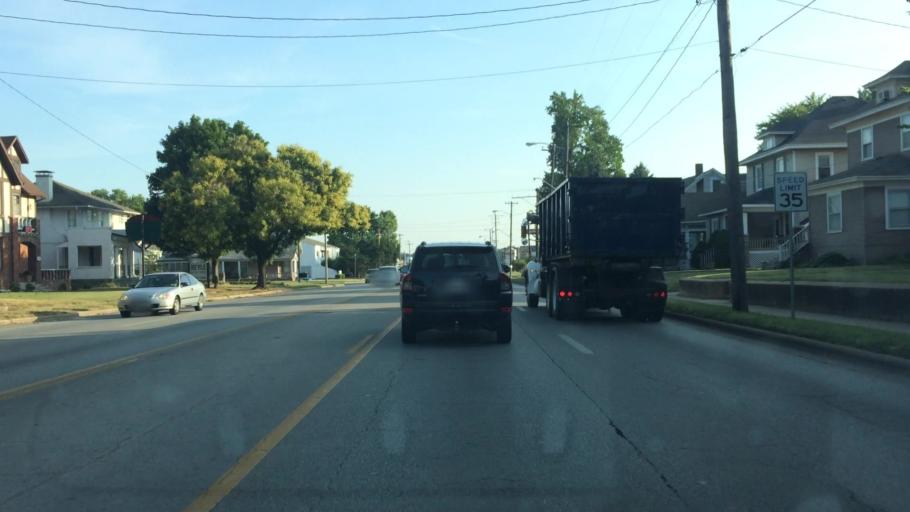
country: US
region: Missouri
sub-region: Greene County
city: Springfield
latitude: 37.2071
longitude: -93.2760
